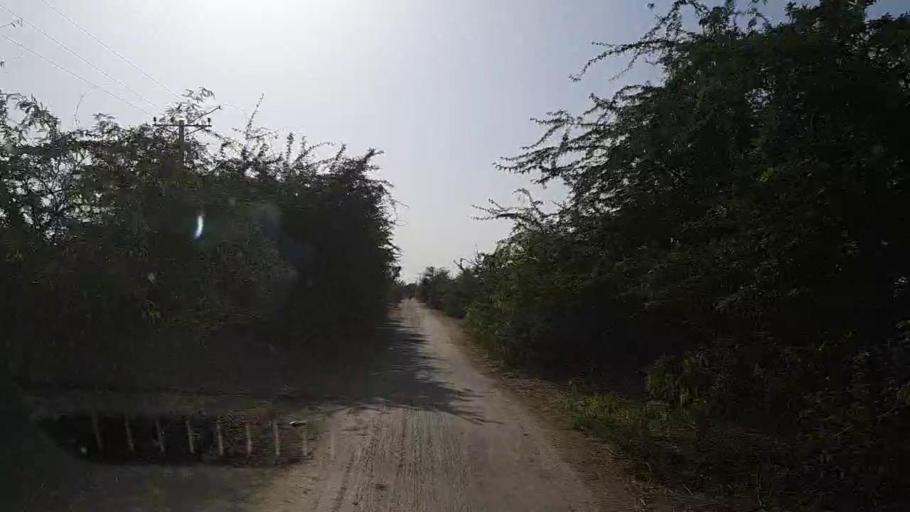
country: PK
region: Sindh
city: Kotri
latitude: 25.1403
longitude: 68.2821
